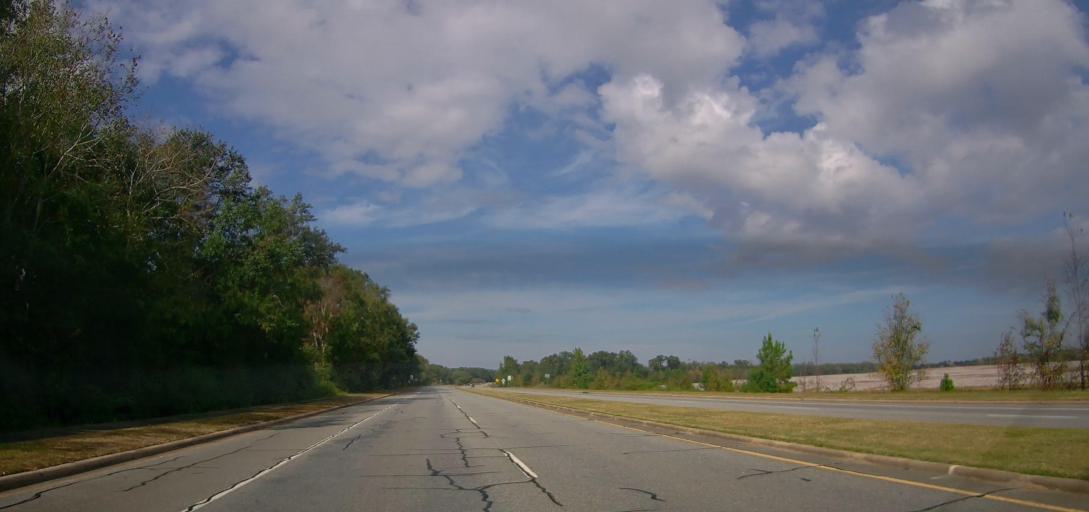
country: US
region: Georgia
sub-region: Mitchell County
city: Camilla
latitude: 31.2401
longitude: -84.2001
